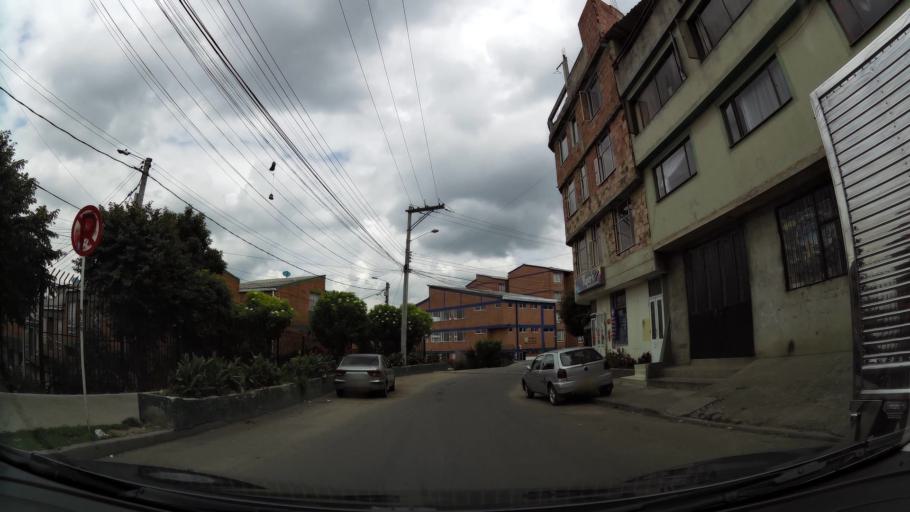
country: CO
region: Cundinamarca
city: La Calera
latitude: 4.7618
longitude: -74.0250
